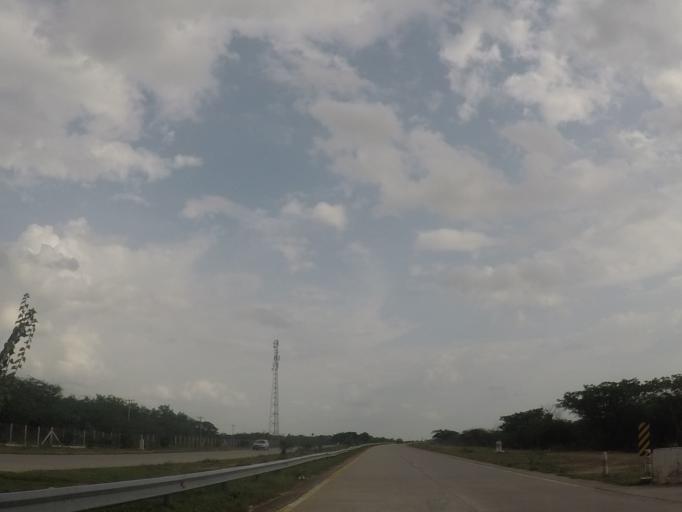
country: MM
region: Mandalay
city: Meiktila
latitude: 20.7786
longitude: 95.7689
